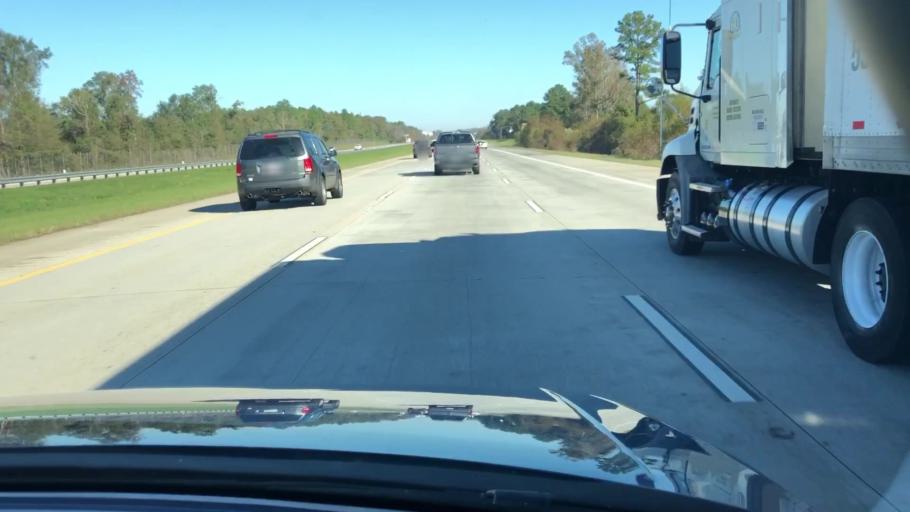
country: US
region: Georgia
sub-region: Dooly County
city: Unadilla
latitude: 32.2191
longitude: -83.7443
